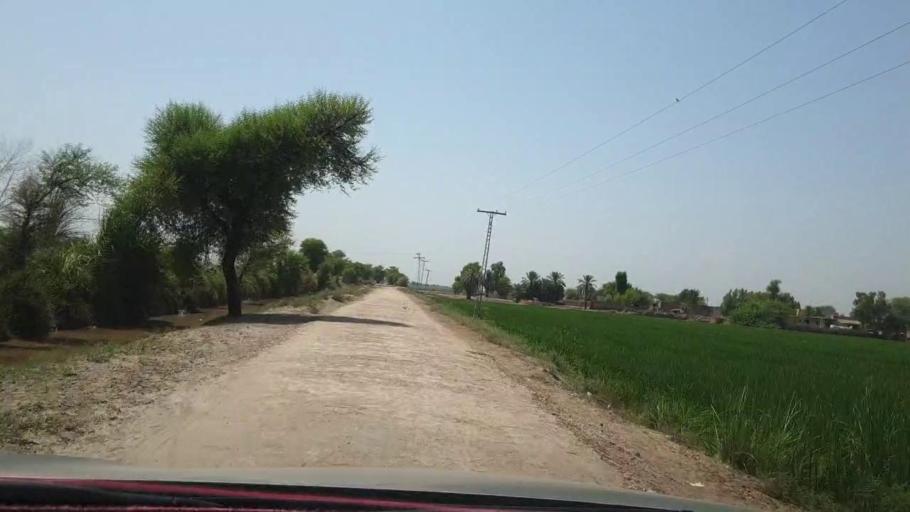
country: PK
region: Sindh
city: Warah
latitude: 27.5021
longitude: 67.7809
